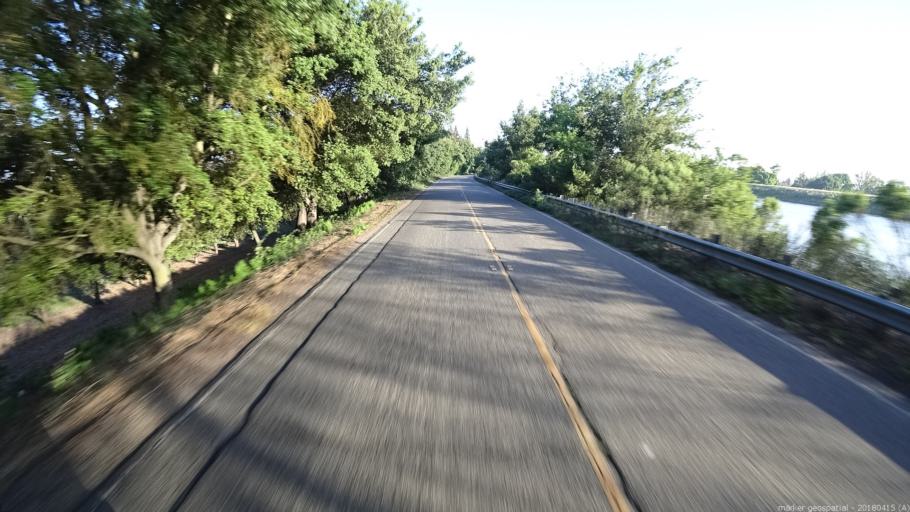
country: US
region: California
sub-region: Sacramento County
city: Walnut Grove
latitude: 38.3100
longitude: -121.5775
